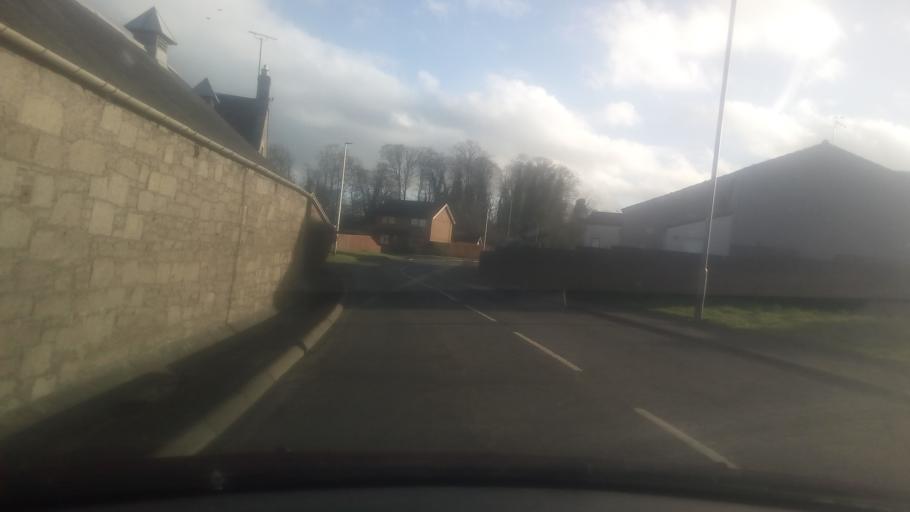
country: GB
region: Scotland
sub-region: The Scottish Borders
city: Kelso
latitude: 55.6097
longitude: -2.4275
